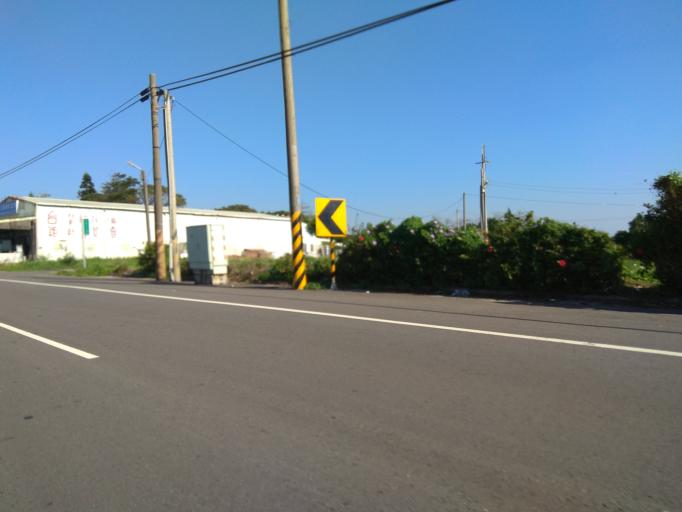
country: TW
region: Taiwan
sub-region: Hsinchu
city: Zhubei
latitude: 25.0211
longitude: 121.0575
